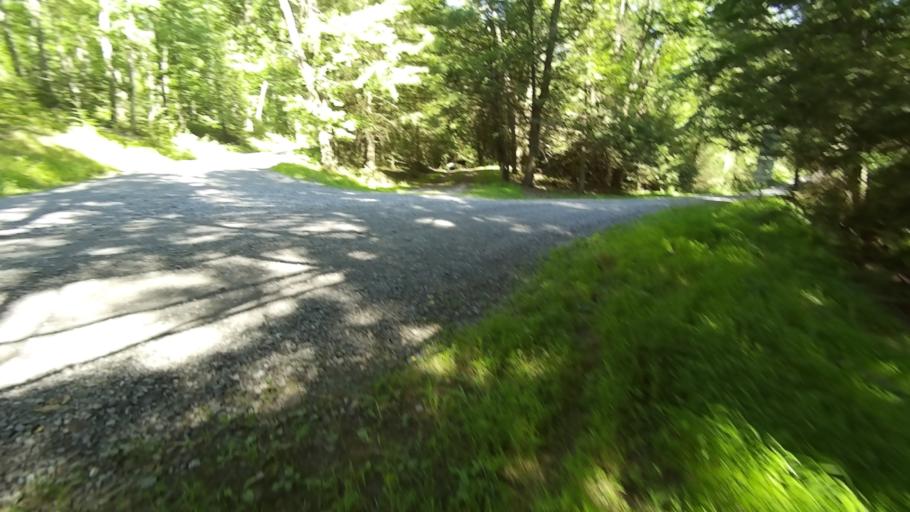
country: US
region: Pennsylvania
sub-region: Centre County
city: Boalsburg
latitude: 40.7332
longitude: -77.7550
